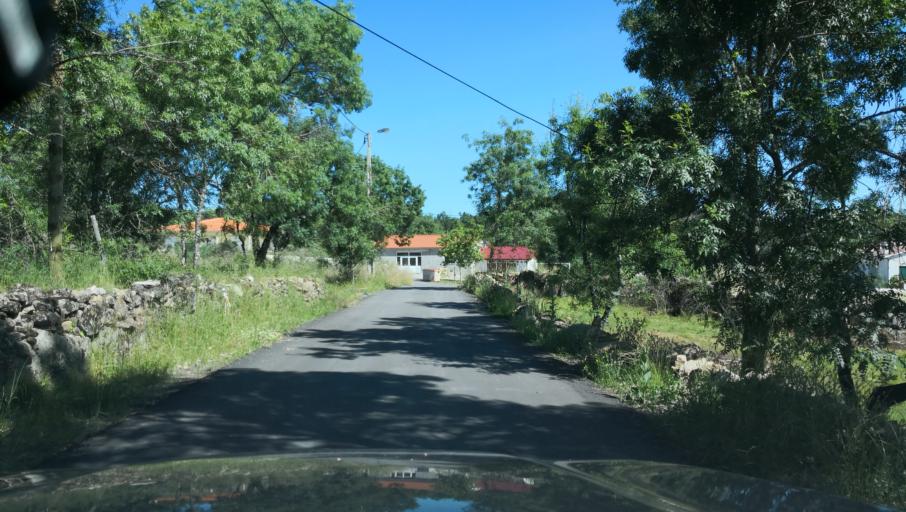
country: PT
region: Vila Real
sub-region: Vila Real
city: Vila Real
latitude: 41.2970
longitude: -7.6763
